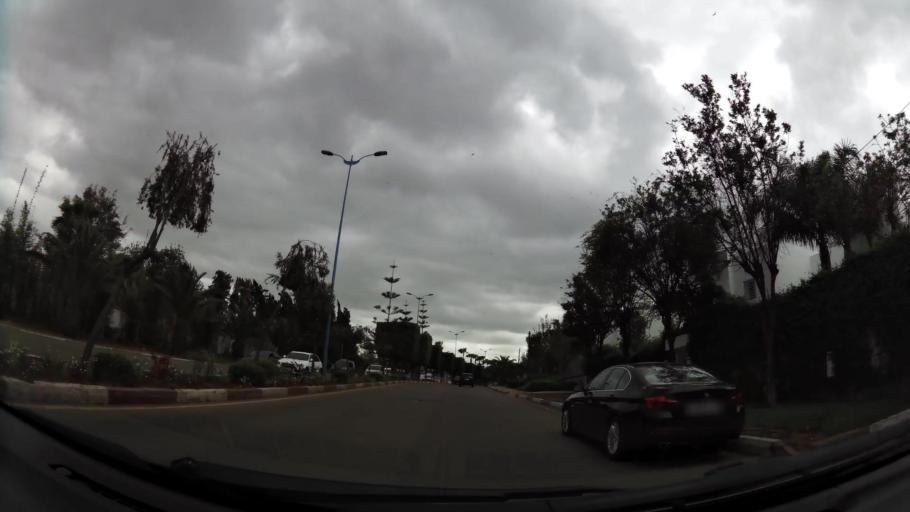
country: MA
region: Grand Casablanca
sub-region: Casablanca
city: Casablanca
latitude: 33.5352
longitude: -7.6300
